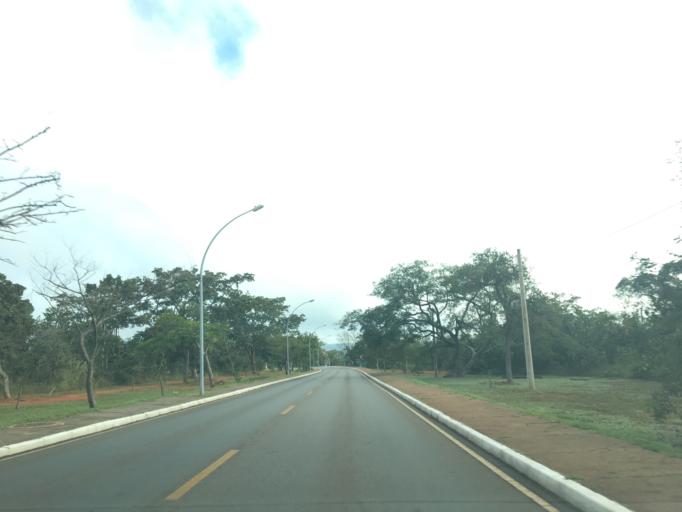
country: BR
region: Federal District
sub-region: Brasilia
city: Brasilia
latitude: -15.8059
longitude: -47.8019
